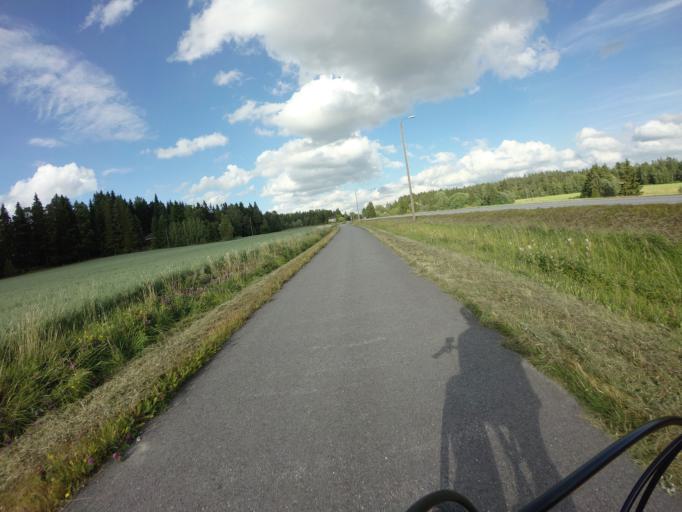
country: FI
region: Varsinais-Suomi
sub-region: Turku
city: Vahto
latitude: 60.5849
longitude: 22.3594
